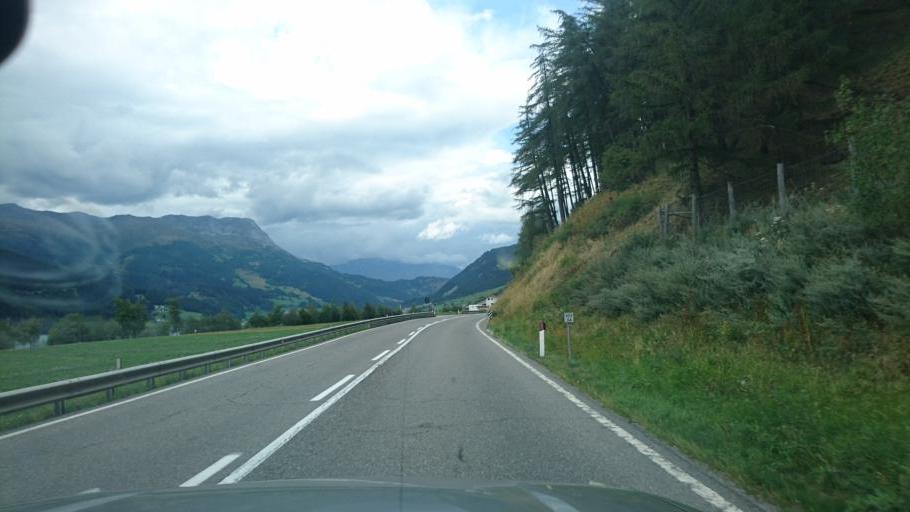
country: IT
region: Trentino-Alto Adige
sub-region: Bolzano
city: Curon Venosta
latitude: 46.8002
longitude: 10.5406
